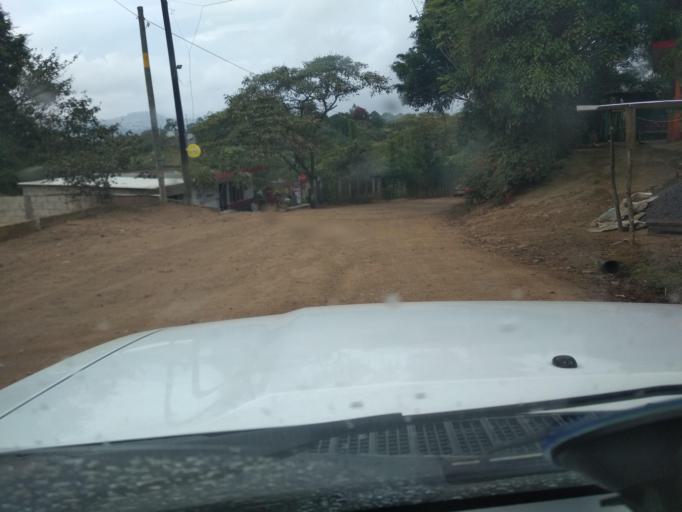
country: MX
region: Veracruz
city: El Castillo
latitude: 19.5396
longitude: -96.8308
